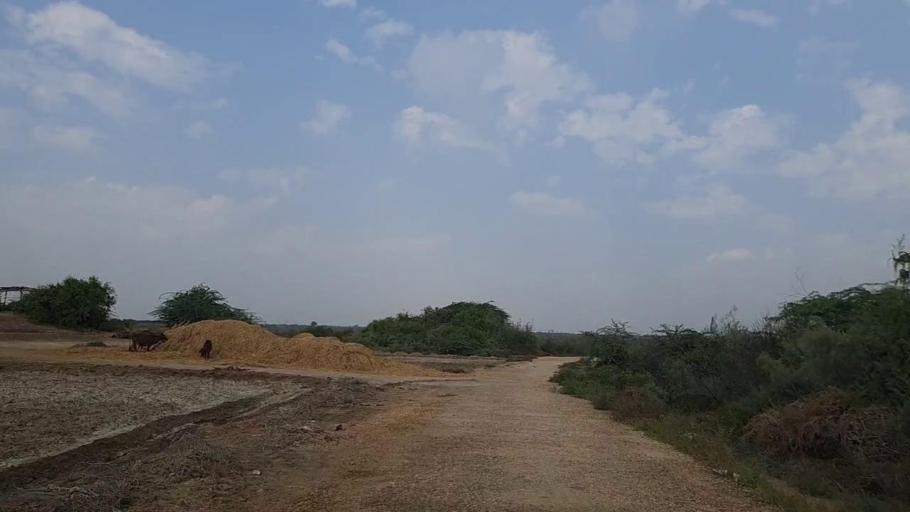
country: PK
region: Sindh
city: Daro Mehar
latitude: 24.6951
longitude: 68.1198
